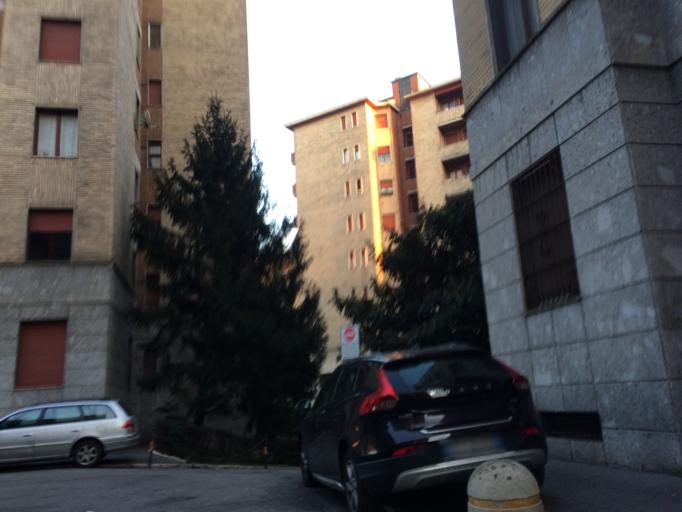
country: IT
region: Lombardy
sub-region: Citta metropolitana di Milano
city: Romano Banco
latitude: 45.4518
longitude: 9.1397
